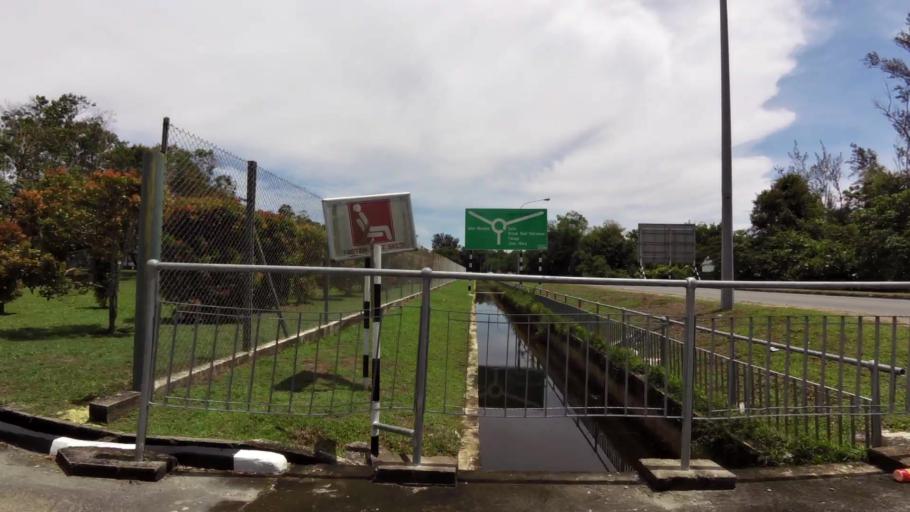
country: BN
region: Belait
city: Kuala Belait
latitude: 4.5932
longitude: 114.2560
